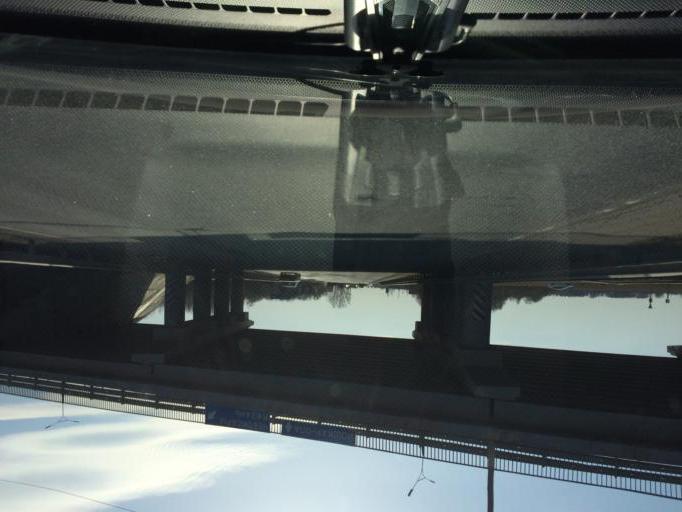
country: RU
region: Mariy-El
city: Yoshkar-Ola
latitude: 56.6797
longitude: 48.0233
